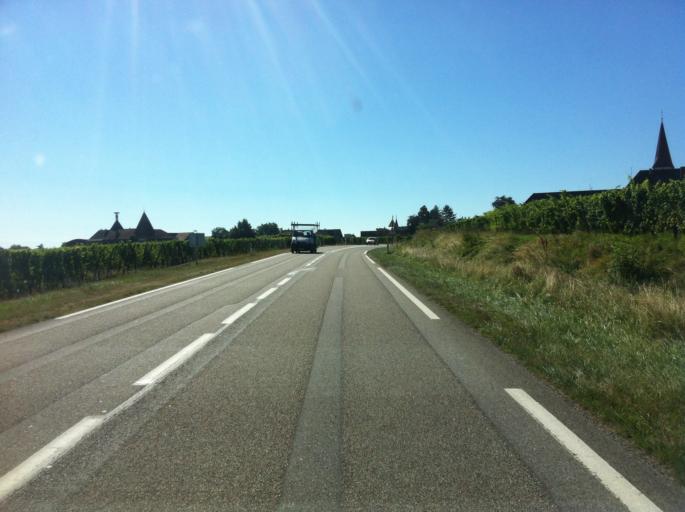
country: FR
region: Alsace
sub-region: Departement du Haut-Rhin
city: Ammerschwihr
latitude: 48.1306
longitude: 7.2808
